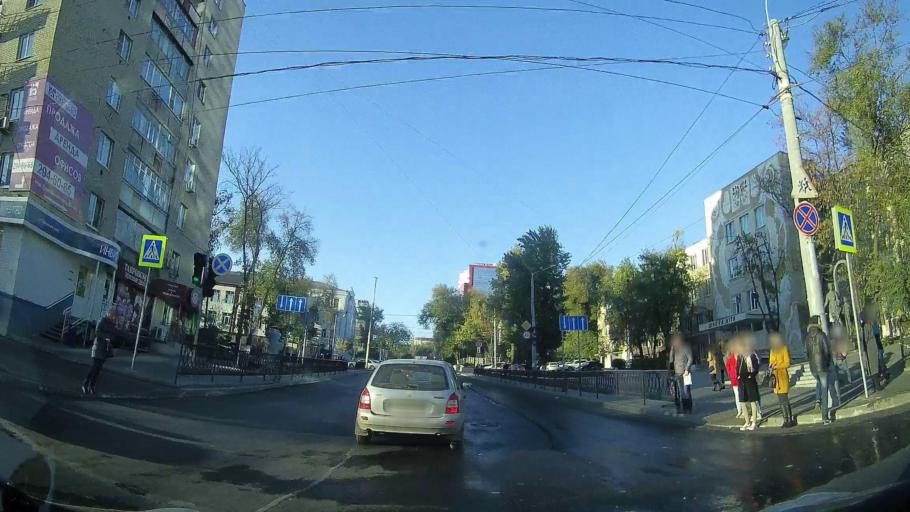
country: RU
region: Rostov
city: Rostov-na-Donu
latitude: 47.2245
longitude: 39.6958
